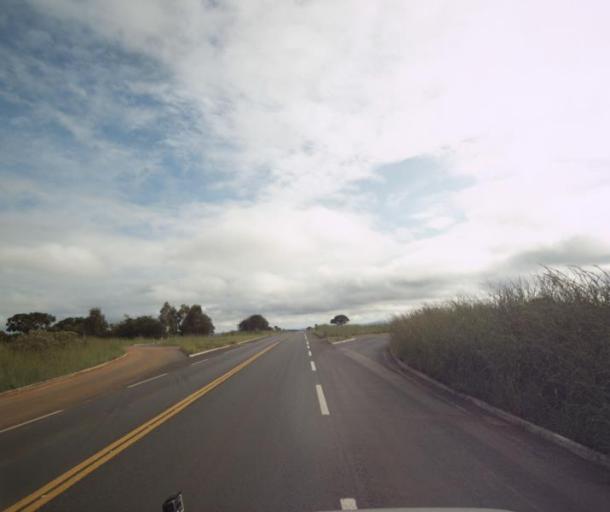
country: BR
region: Goias
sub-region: Padre Bernardo
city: Padre Bernardo
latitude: -15.3582
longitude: -48.6465
